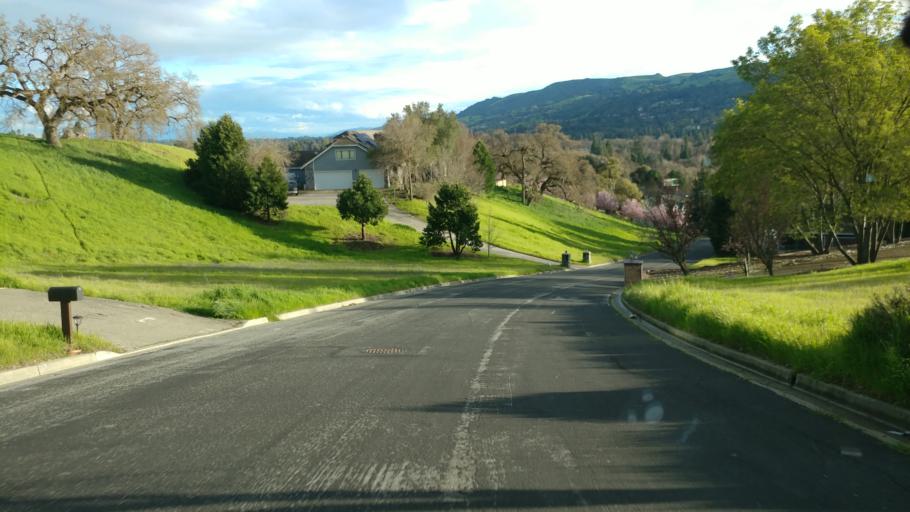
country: US
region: California
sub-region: Contra Costa County
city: Danville
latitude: 37.8363
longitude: -122.0067
